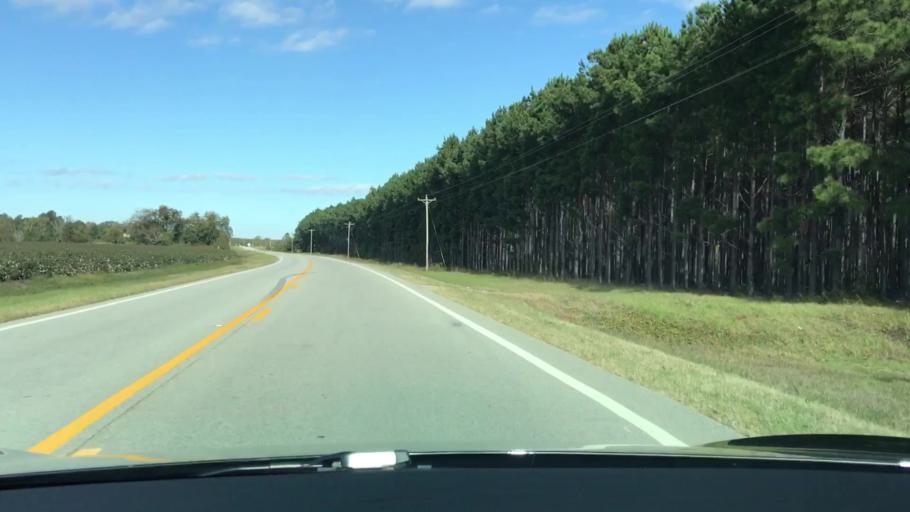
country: US
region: Georgia
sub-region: Glascock County
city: Gibson
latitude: 33.2847
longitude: -82.5059
